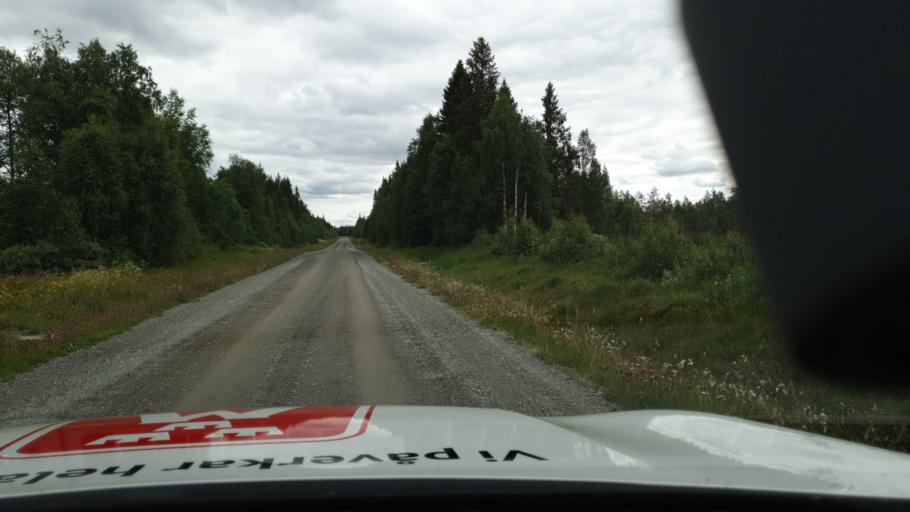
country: SE
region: Vaesterbotten
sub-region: Storumans Kommun
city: Storuman
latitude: 64.7255
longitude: 17.0740
